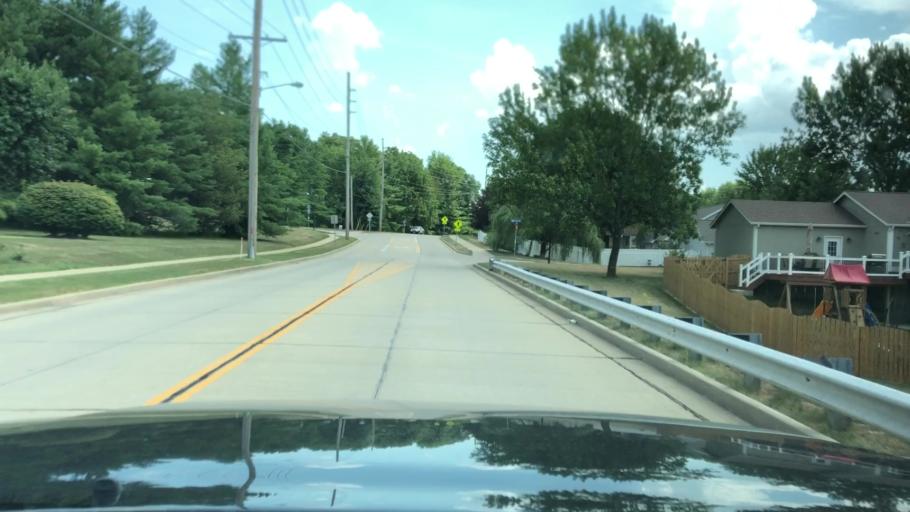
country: US
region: Missouri
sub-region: Saint Charles County
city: Saint Charles
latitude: 38.8073
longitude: -90.5365
